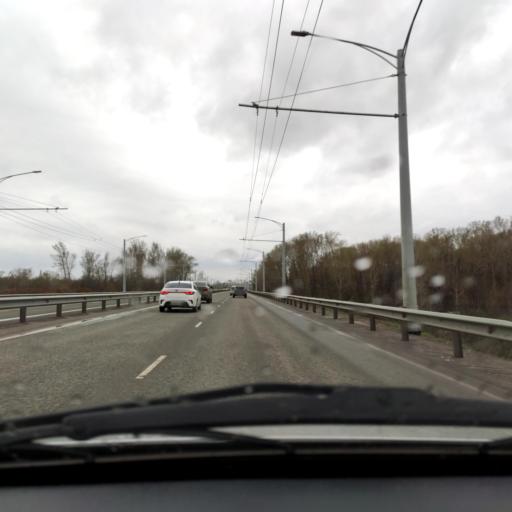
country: RU
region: Bashkortostan
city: Mikhaylovka
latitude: 54.7731
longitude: 55.9022
